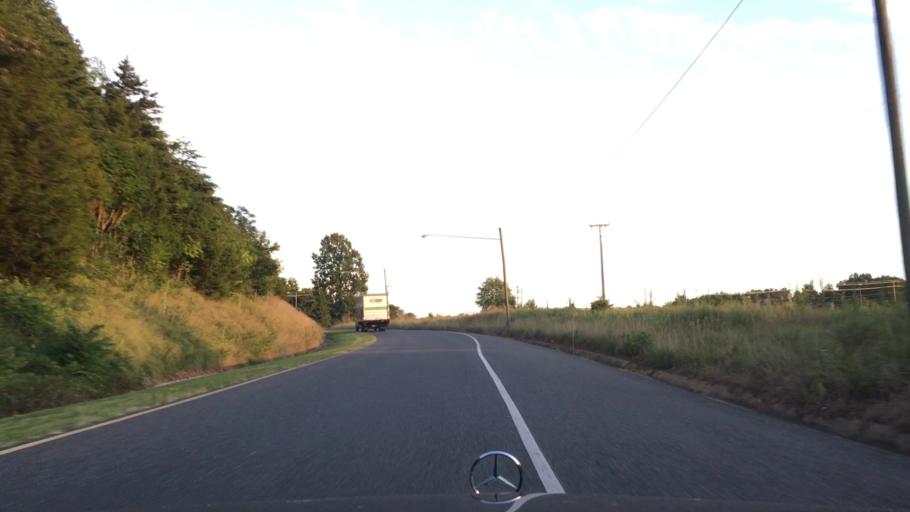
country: US
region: Virginia
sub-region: City of Lynchburg
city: West Lynchburg
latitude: 37.3787
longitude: -79.2223
